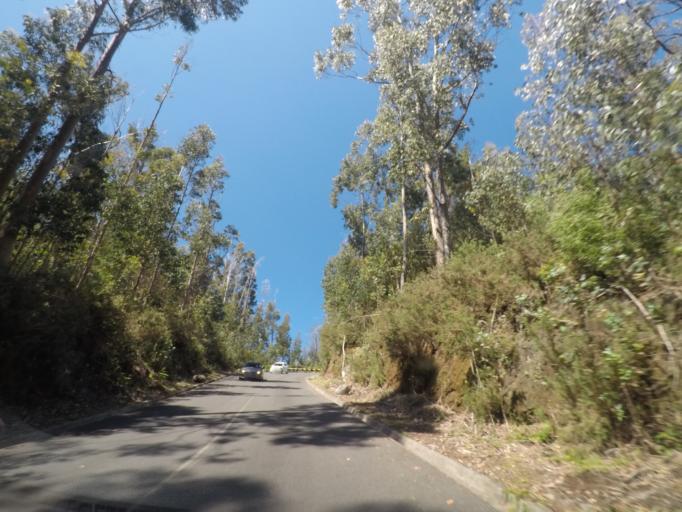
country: PT
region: Madeira
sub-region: Calheta
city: Arco da Calheta
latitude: 32.7391
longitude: -17.1285
